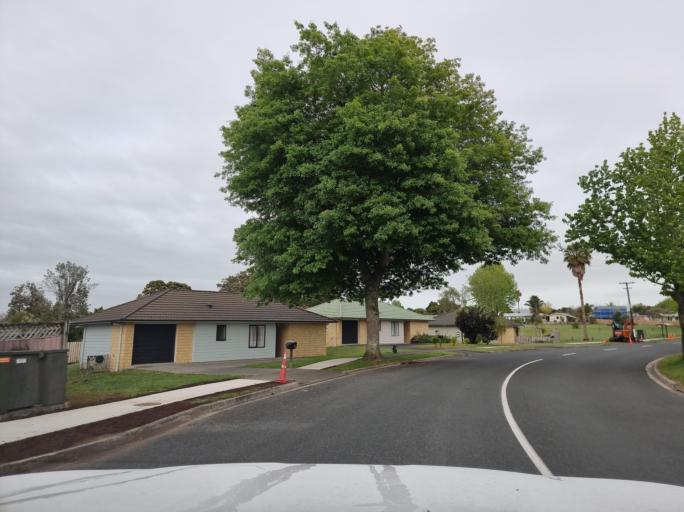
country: NZ
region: Northland
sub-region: Whangarei
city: Whangarei
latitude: -35.7523
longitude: 174.3659
